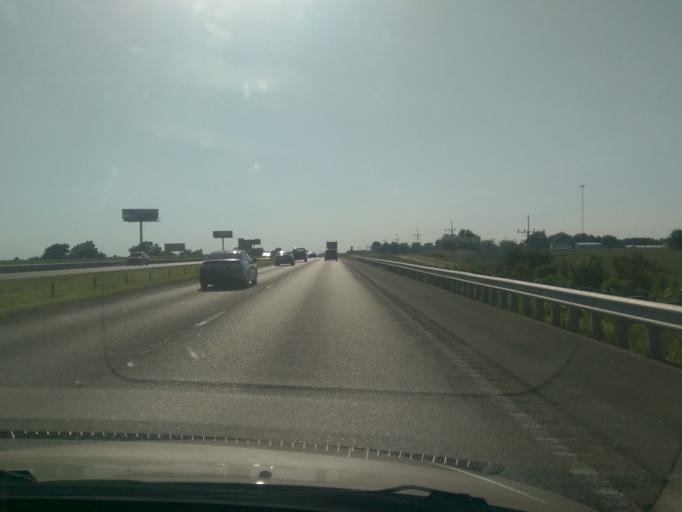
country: US
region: Missouri
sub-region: Lafayette County
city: Higginsville
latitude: 39.0015
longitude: -93.7555
